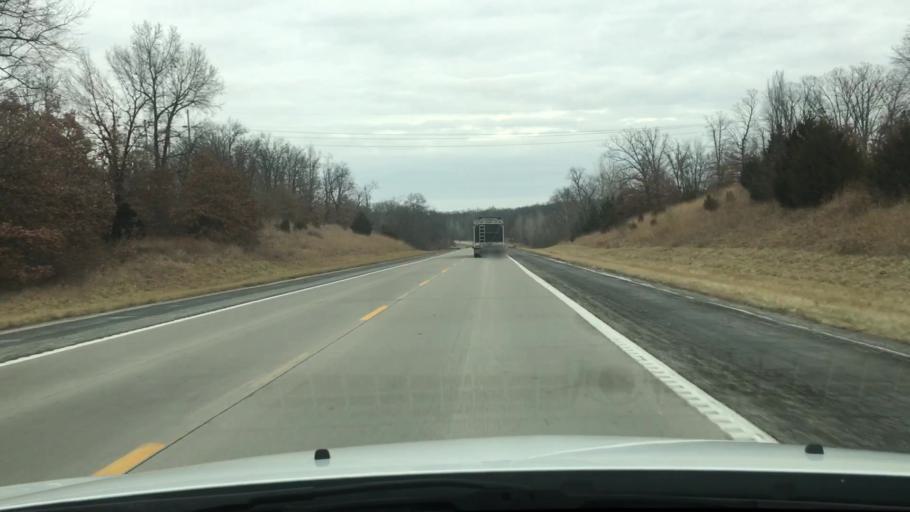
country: US
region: Missouri
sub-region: Audrain County
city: Mexico
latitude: 39.1416
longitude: -91.8483
